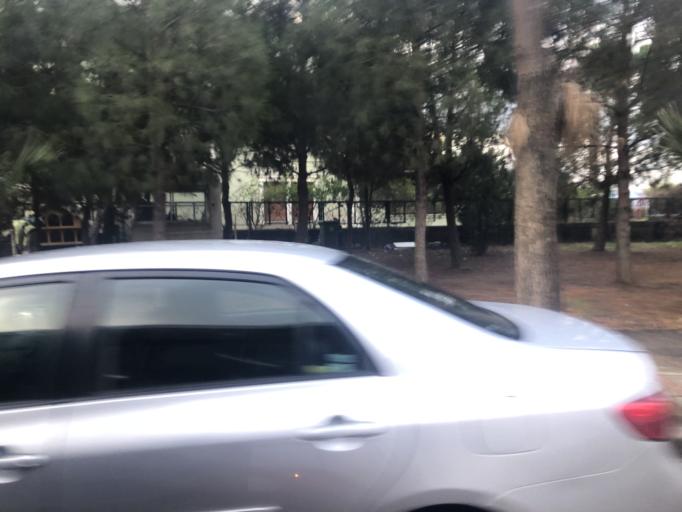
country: TR
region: Izmir
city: Karsiyaka
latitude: 38.4678
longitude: 27.0670
